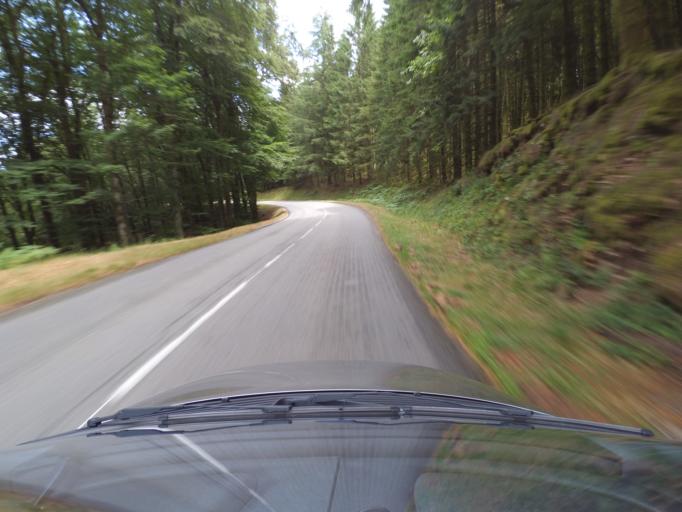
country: FR
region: Limousin
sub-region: Departement de la Creuse
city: Bourganeuf
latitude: 45.9036
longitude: 1.8593
